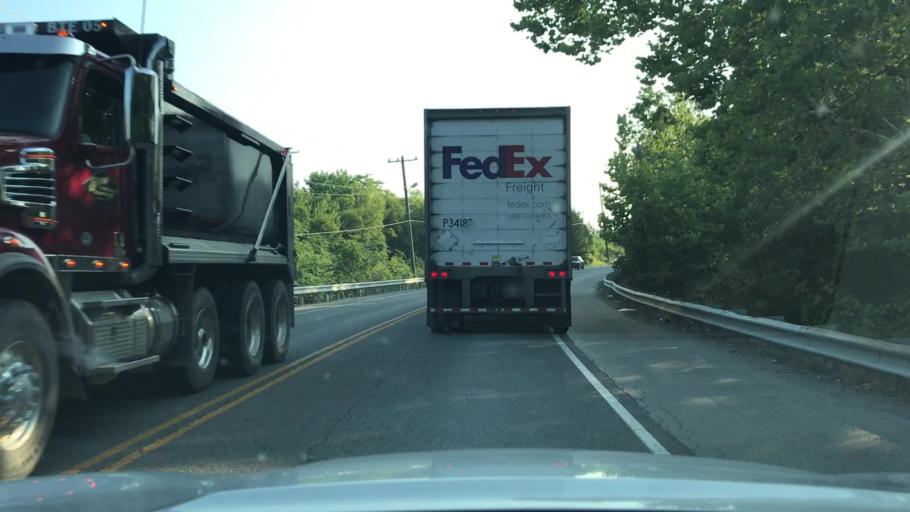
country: US
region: Tennessee
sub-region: Rutherford County
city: La Vergne
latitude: 36.0406
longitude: -86.6098
